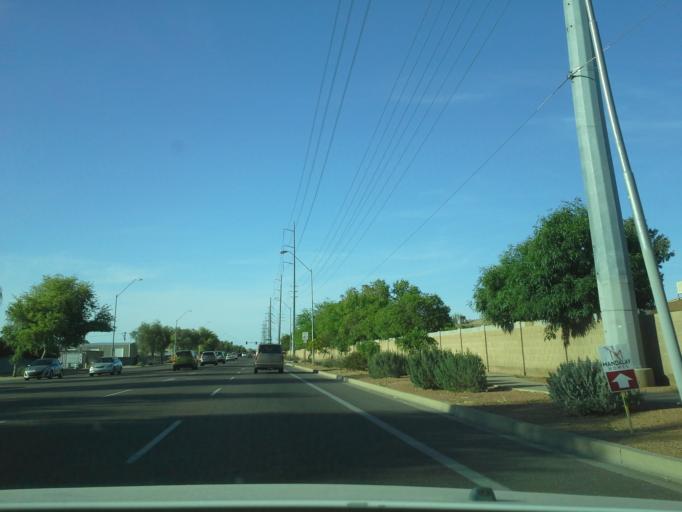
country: US
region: Arizona
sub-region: Maricopa County
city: Peoria
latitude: 33.6591
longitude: -112.1344
